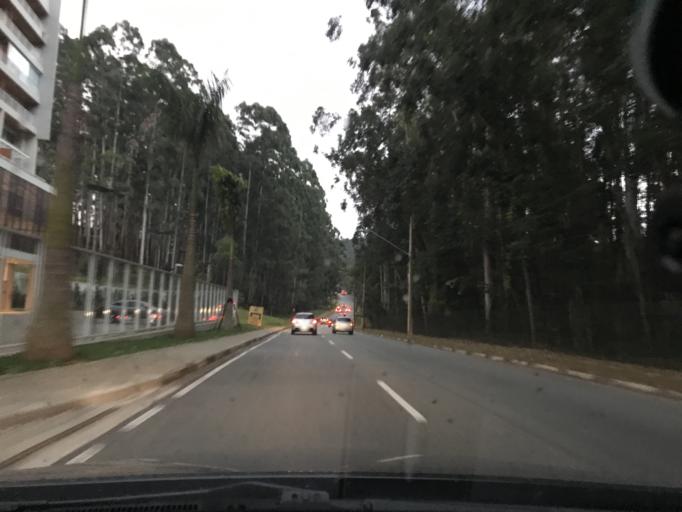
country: BR
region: Sao Paulo
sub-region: Carapicuiba
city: Carapicuiba
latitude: -23.4718
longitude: -46.8413
